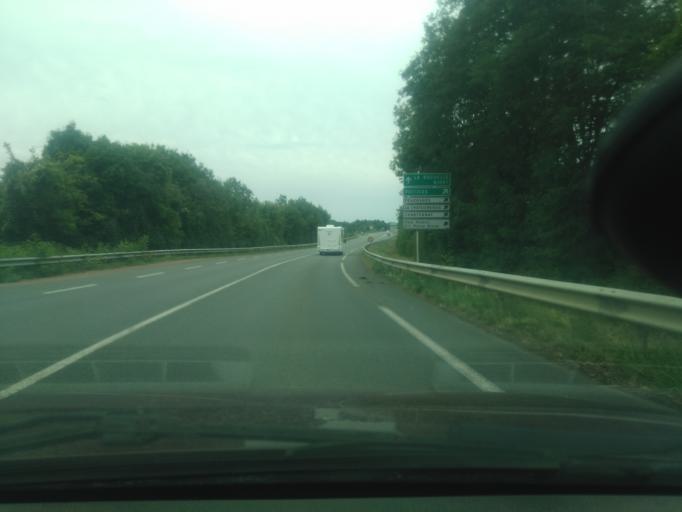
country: FR
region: Pays de la Loire
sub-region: Departement de la Vendee
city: Chantonnay
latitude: 46.7001
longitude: -1.0601
